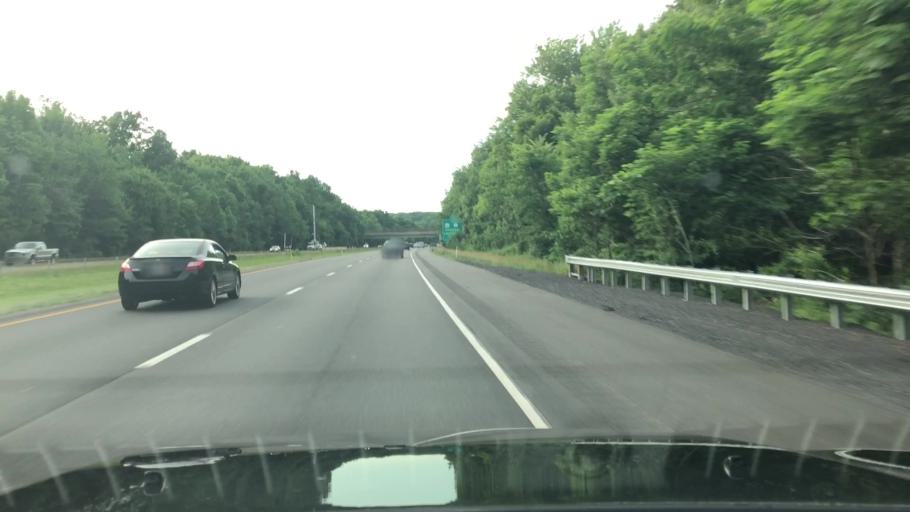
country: US
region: Pennsylvania
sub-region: Bucks County
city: Hulmeville
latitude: 40.1536
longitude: -74.8992
